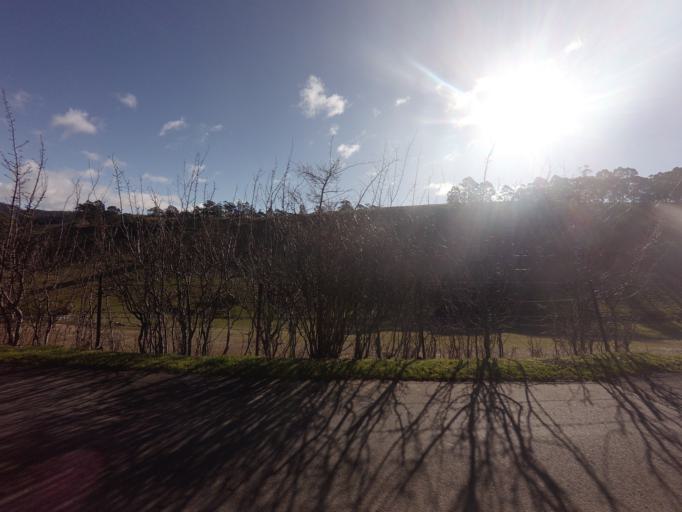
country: AU
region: Tasmania
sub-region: Glenorchy
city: Berriedale
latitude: -42.8339
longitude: 147.2027
